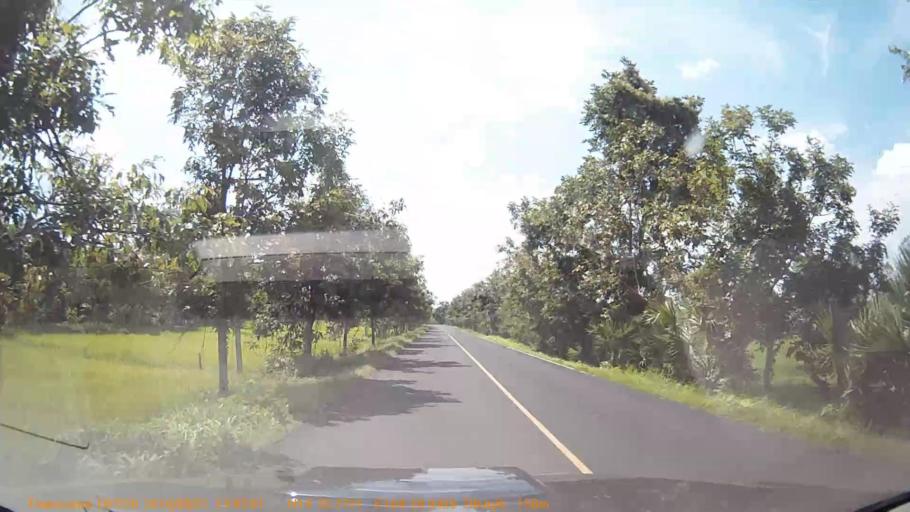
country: TH
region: Sisaket
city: Khun Han
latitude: 14.5464
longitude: 104.4668
